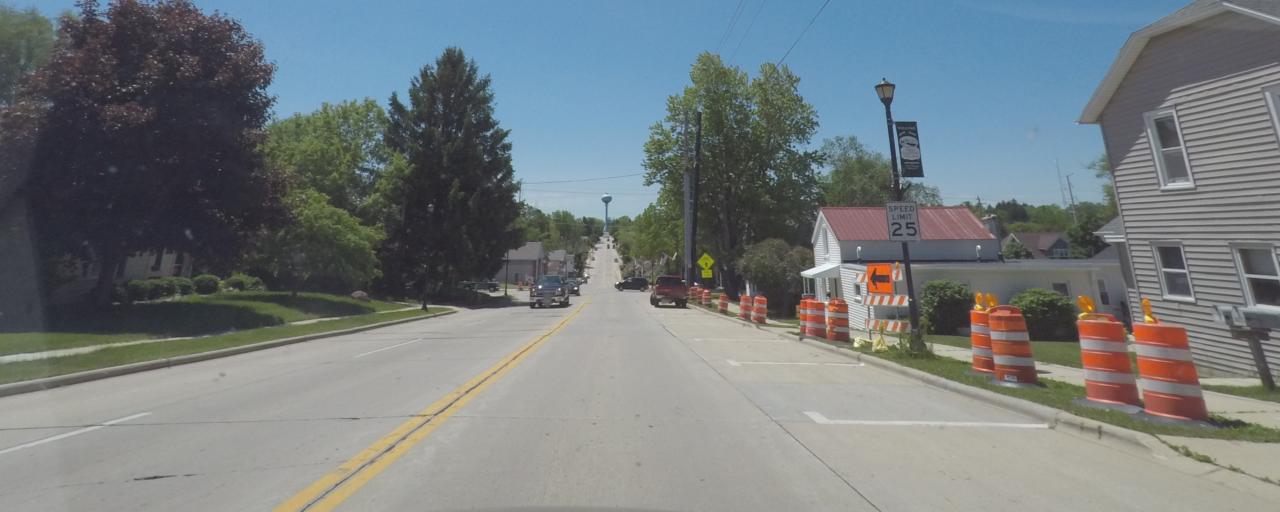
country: US
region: Wisconsin
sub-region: Washington County
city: West Bend
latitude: 43.4439
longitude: -88.1789
